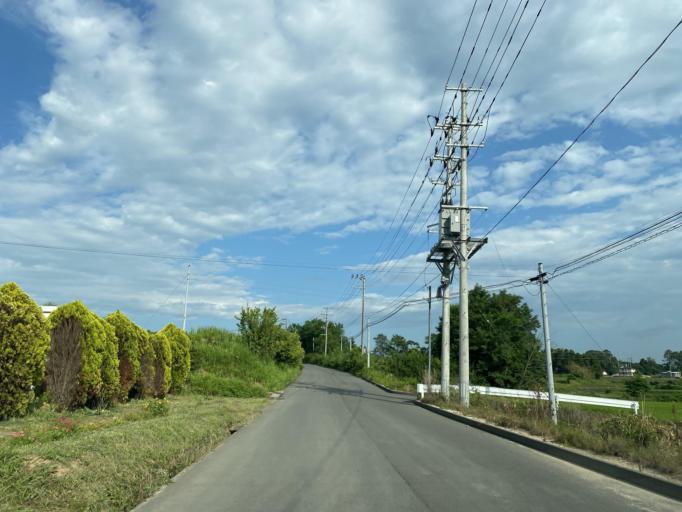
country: JP
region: Fukushima
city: Koriyama
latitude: 37.3492
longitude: 140.3427
